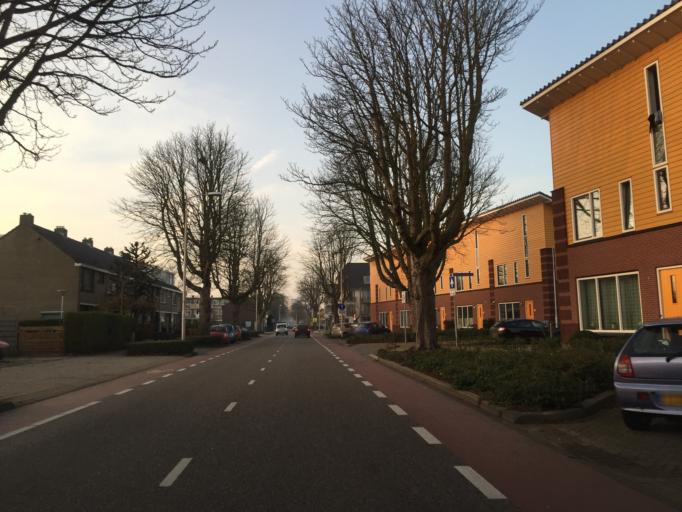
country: NL
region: South Holland
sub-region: Gemeente Zoetermeer
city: Zoetermeer
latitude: 52.0494
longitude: 4.5024
